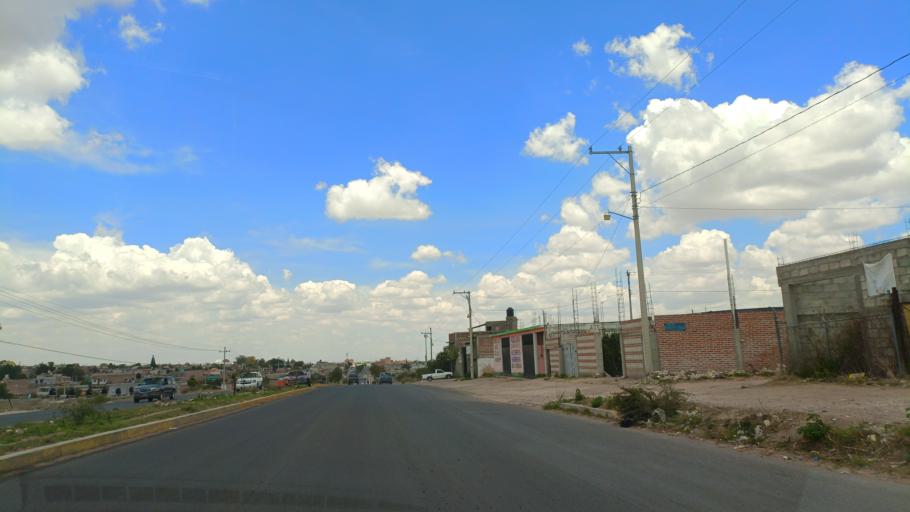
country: MX
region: Guerrero
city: San Luis de la Paz
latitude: 21.2897
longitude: -100.4999
